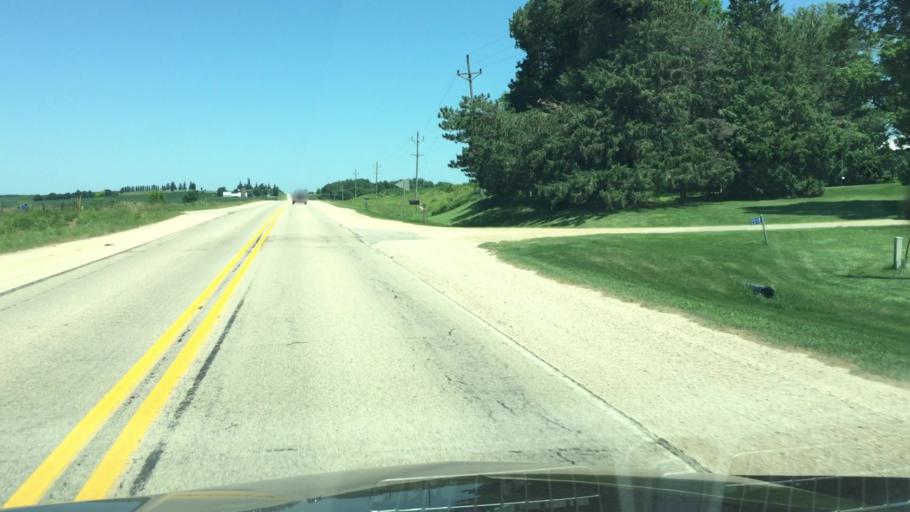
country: US
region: Iowa
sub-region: Cedar County
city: Mechanicsville
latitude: 41.9655
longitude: -91.1421
